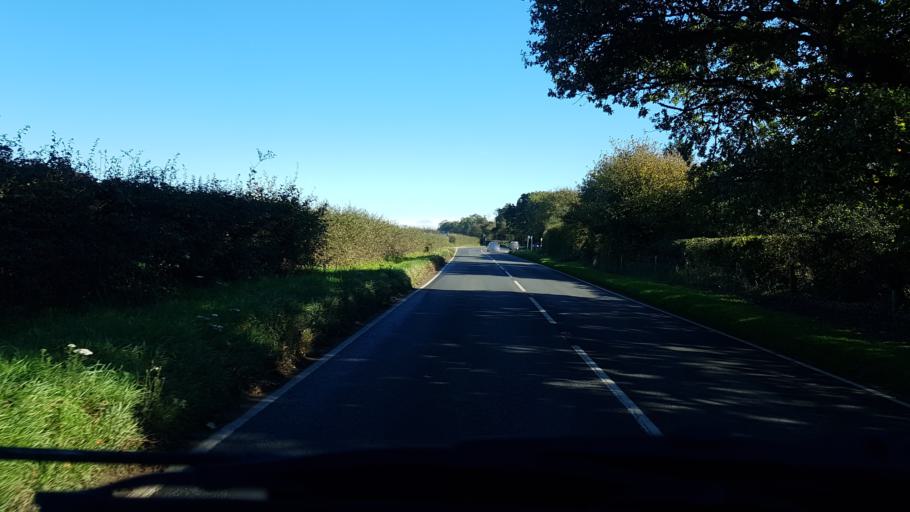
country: GB
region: England
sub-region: Surrey
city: East Horsley
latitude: 51.2147
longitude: -0.4026
